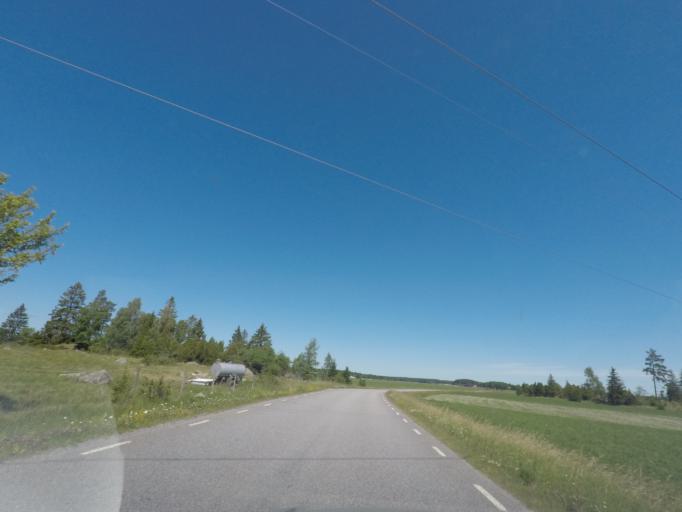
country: SE
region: Uppsala
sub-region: Enkopings Kommun
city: Irsta
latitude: 59.6865
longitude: 16.9602
